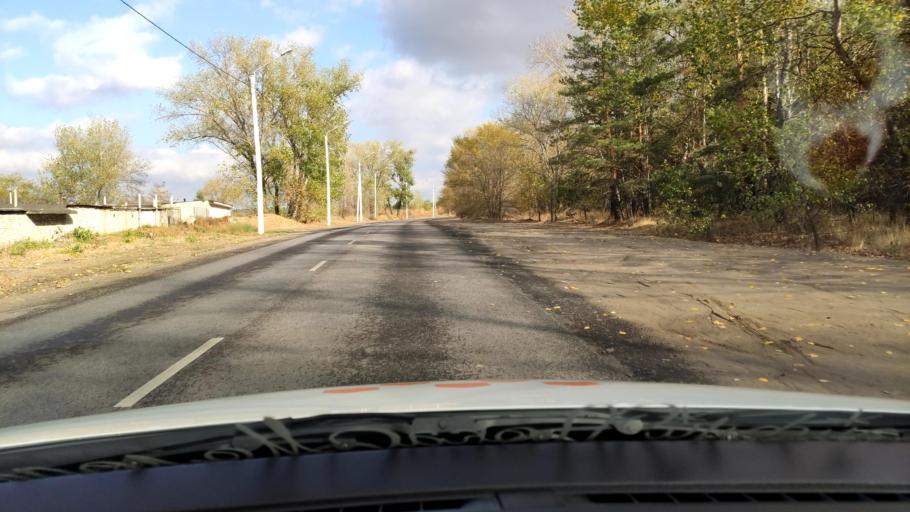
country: RU
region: Voronezj
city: Pridonskoy
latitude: 51.6898
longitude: 39.0815
